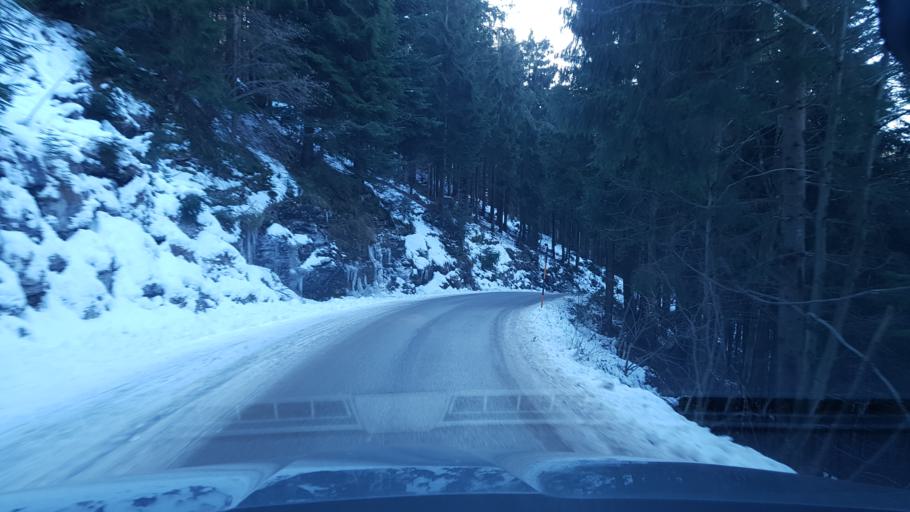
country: AT
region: Salzburg
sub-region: Politischer Bezirk Hallein
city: Scheffau am Tennengebirge
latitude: 47.6364
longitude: 13.2366
